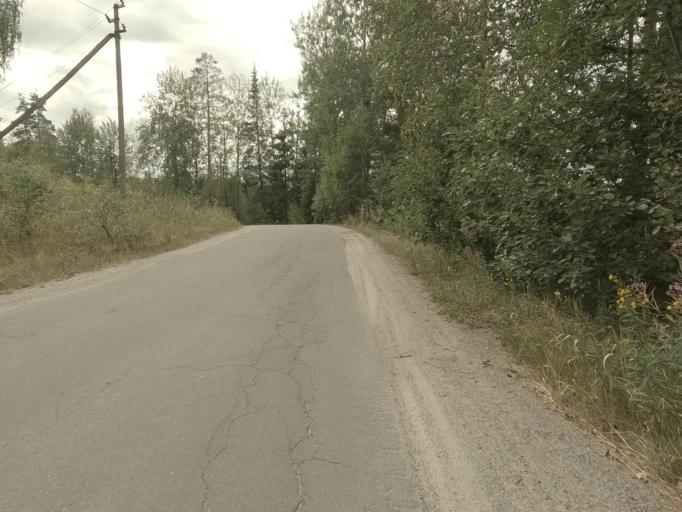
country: RU
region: Leningrad
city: Kamennogorsk
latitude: 60.9734
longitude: 29.1702
